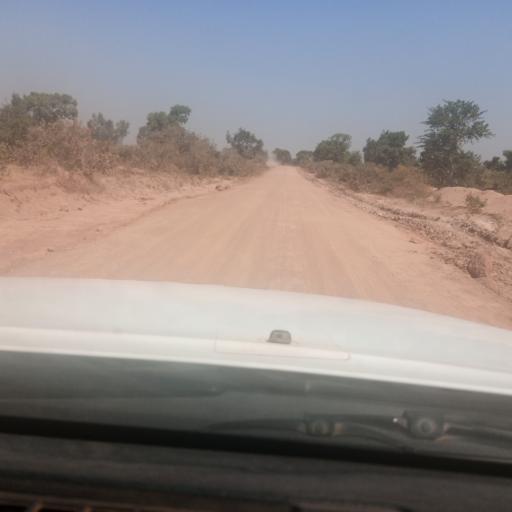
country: NG
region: Adamawa
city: Yola
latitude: 9.0949
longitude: 12.3898
